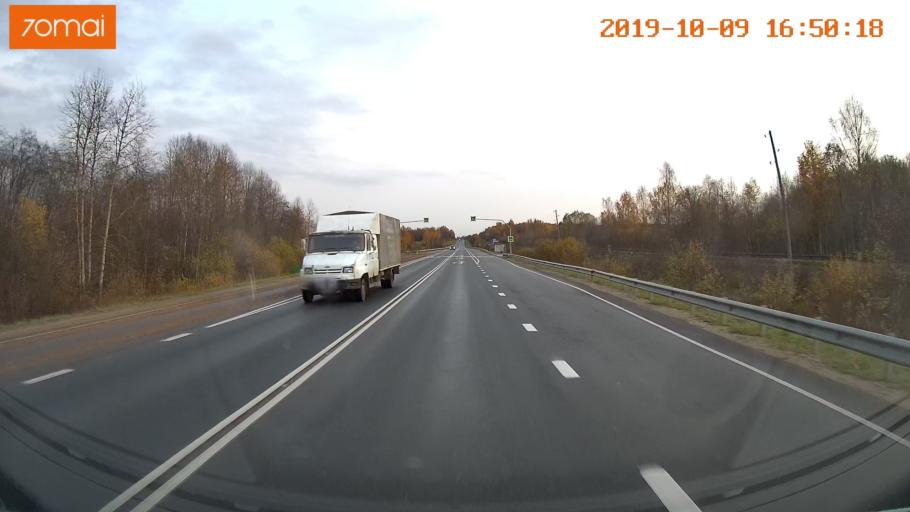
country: RU
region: Kostroma
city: Volgorechensk
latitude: 57.4028
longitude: 41.2071
